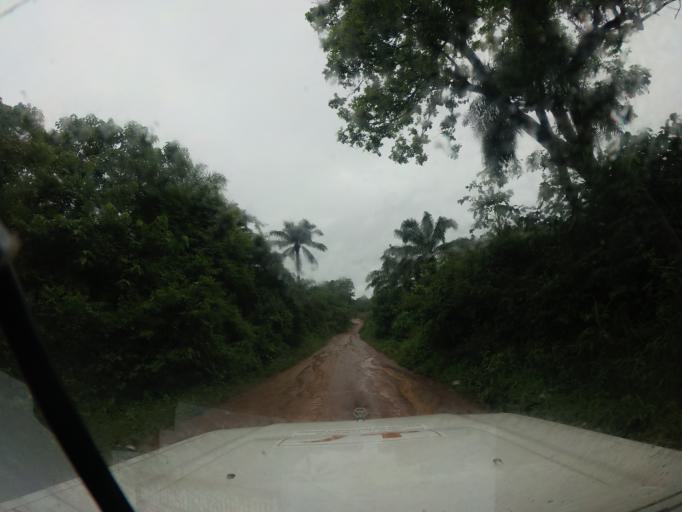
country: SL
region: Northern Province
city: Kabala
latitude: 9.6300
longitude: -11.5493
